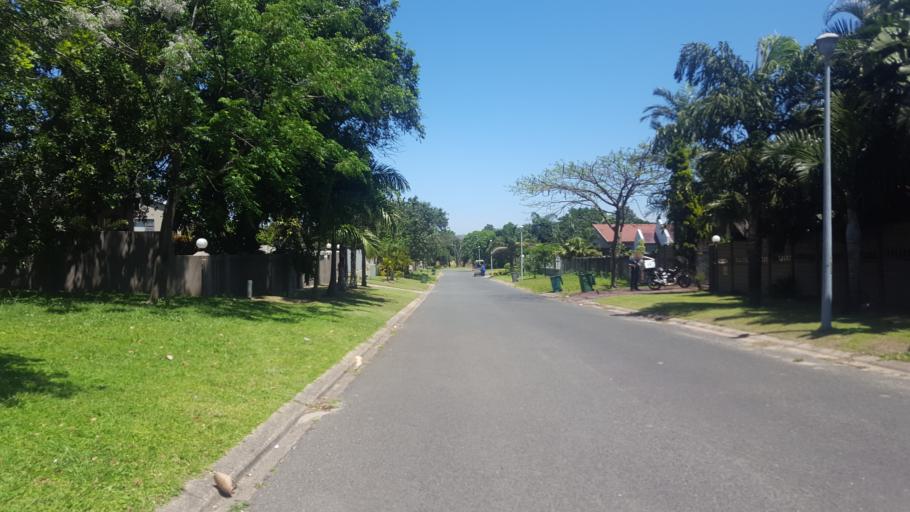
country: ZA
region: KwaZulu-Natal
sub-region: uThungulu District Municipality
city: Richards Bay
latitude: -28.7640
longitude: 32.0635
